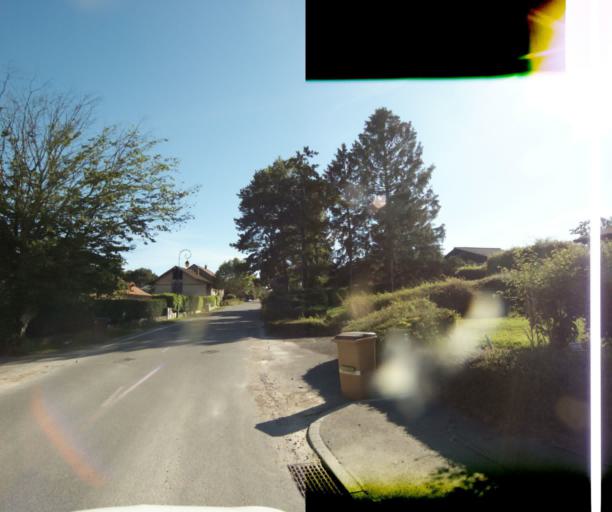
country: FR
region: Rhone-Alpes
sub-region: Departement de la Haute-Savoie
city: Massongy
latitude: 46.3508
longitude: 6.3332
